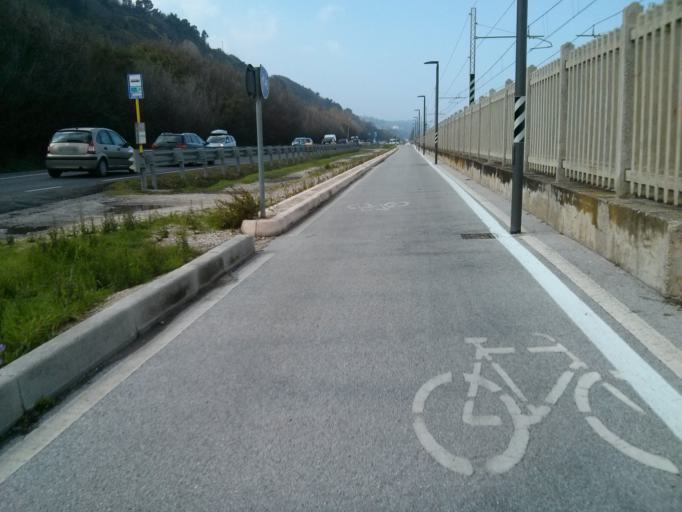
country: IT
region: The Marches
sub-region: Provincia di Pesaro e Urbino
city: Fenile
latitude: 43.8729
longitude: 12.9741
